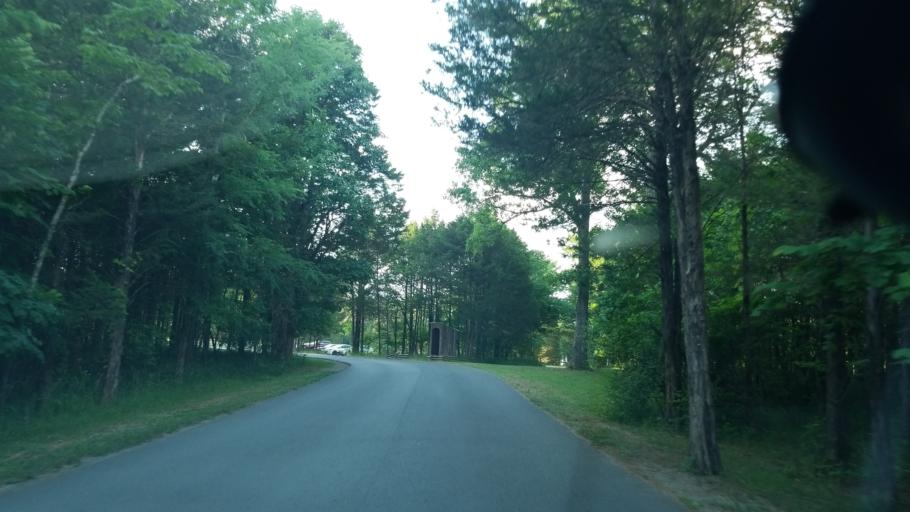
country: US
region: Tennessee
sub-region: Rutherford County
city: La Vergne
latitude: 36.0870
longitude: -86.5880
